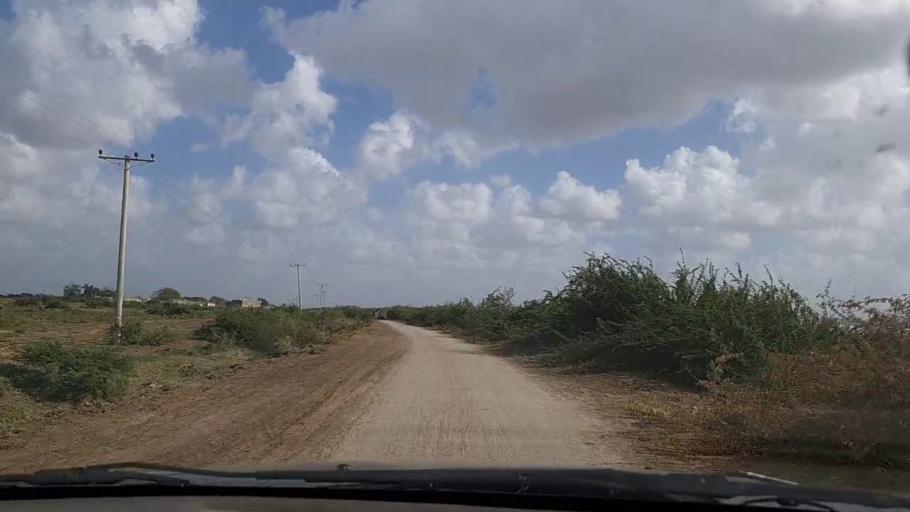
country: PK
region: Sindh
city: Keti Bandar
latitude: 24.0937
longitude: 67.6119
